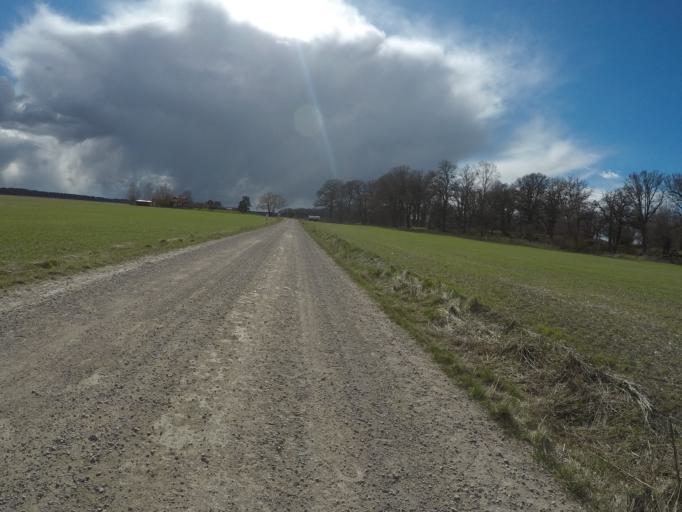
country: SE
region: Vaestmanland
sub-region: Hallstahammars Kommun
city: Kolback
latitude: 59.5191
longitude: 16.2449
